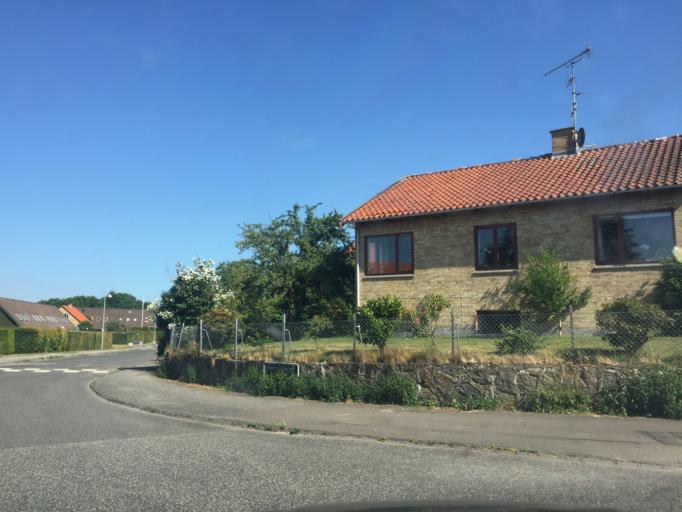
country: DK
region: Capital Region
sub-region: Ballerup Kommune
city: Malov
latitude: 55.7847
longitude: 12.3233
